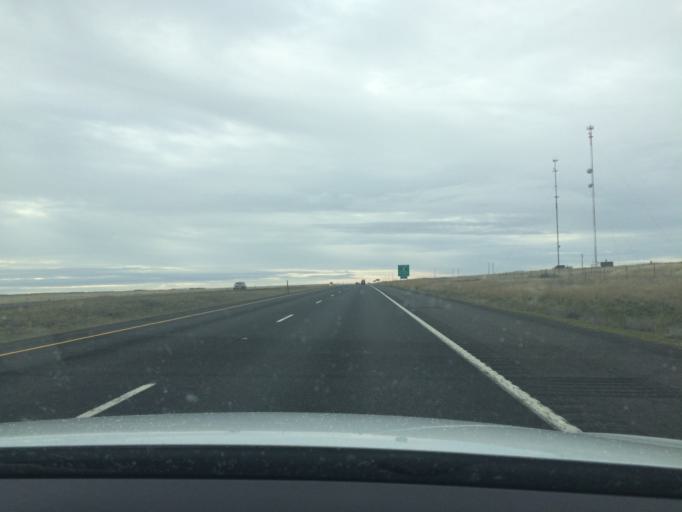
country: US
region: Washington
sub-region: Spokane County
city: Medical Lake
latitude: 47.3203
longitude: -117.9488
